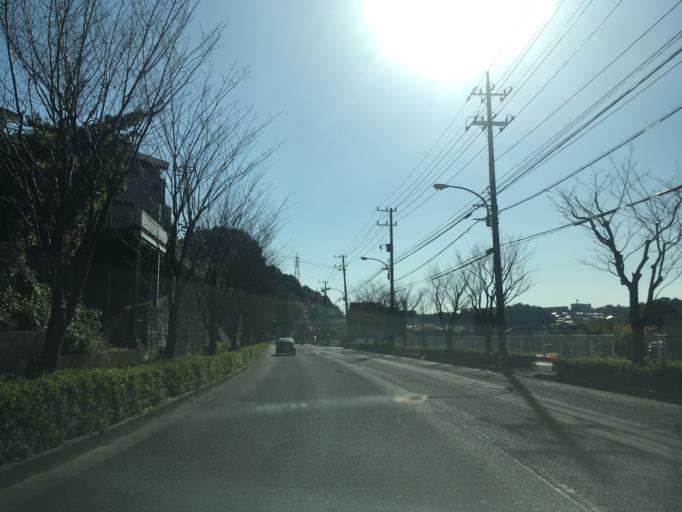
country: JP
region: Tokyo
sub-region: Machida-shi
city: Machida
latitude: 35.5881
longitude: 139.4194
